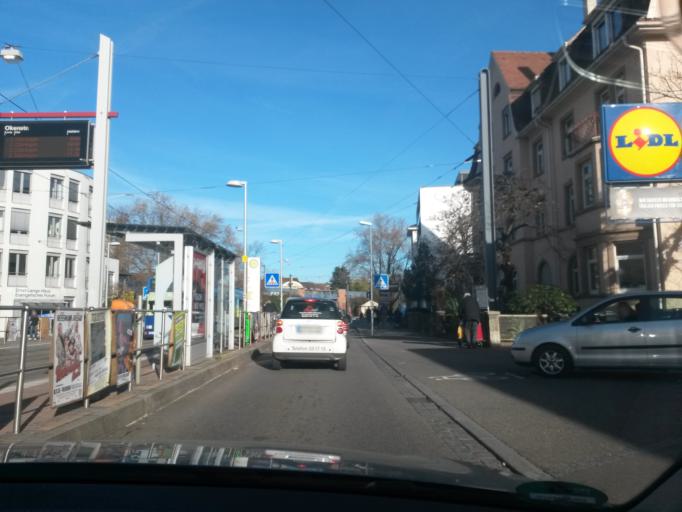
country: DE
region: Baden-Wuerttemberg
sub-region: Freiburg Region
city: Freiburg
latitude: 48.0106
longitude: 7.8546
